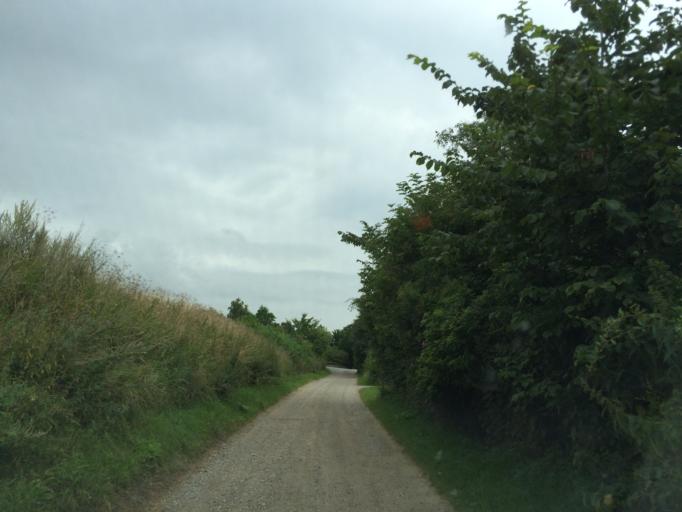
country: DK
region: Central Jutland
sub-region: Syddjurs Kommune
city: Ronde
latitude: 56.2399
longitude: 10.5550
